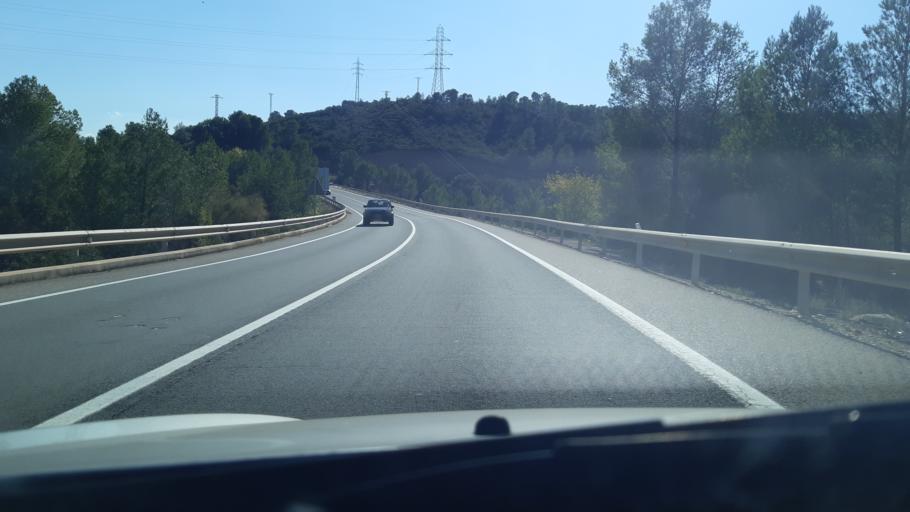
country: ES
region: Catalonia
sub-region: Provincia de Tarragona
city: Tivenys
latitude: 40.9310
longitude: 0.4847
